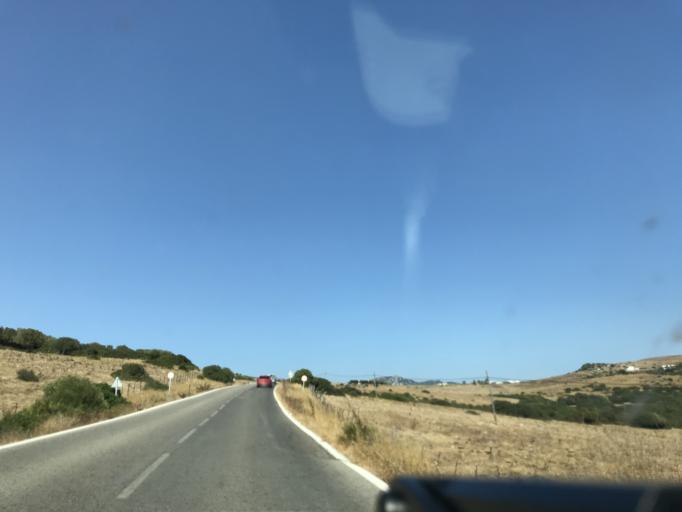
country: ES
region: Andalusia
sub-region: Provincia de Cadiz
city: Zahara de los Atunes
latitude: 36.1007
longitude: -5.7462
